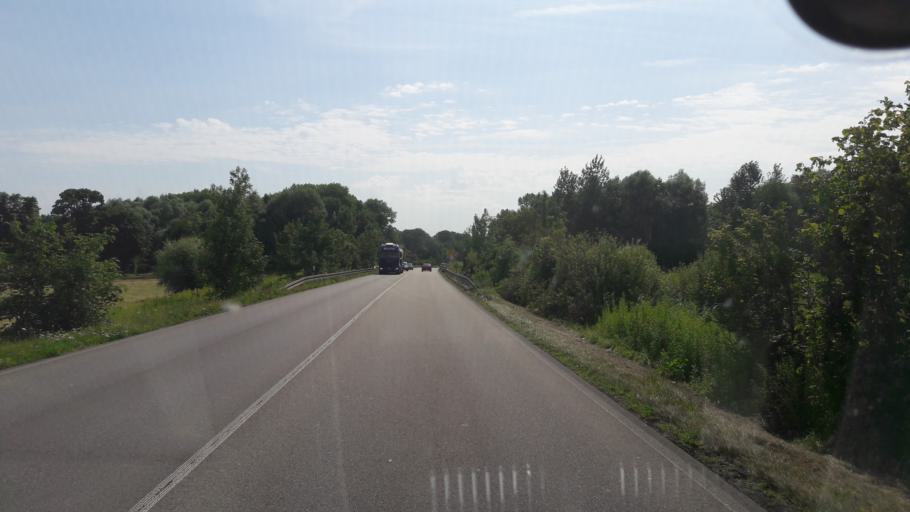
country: DE
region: Baden-Wuerttemberg
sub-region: Freiburg Region
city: Appenweier
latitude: 48.5333
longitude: 7.9500
